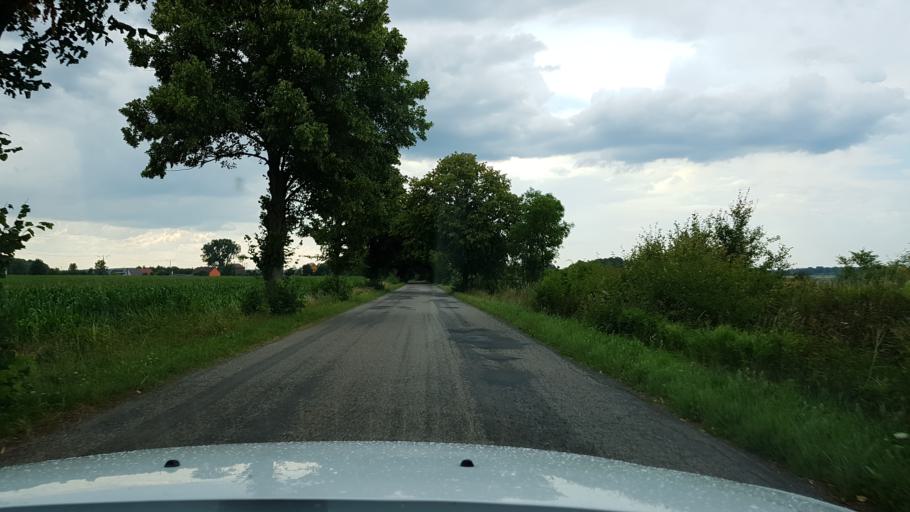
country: PL
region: West Pomeranian Voivodeship
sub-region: Powiat walecki
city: Walcz
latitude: 53.3489
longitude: 16.3706
